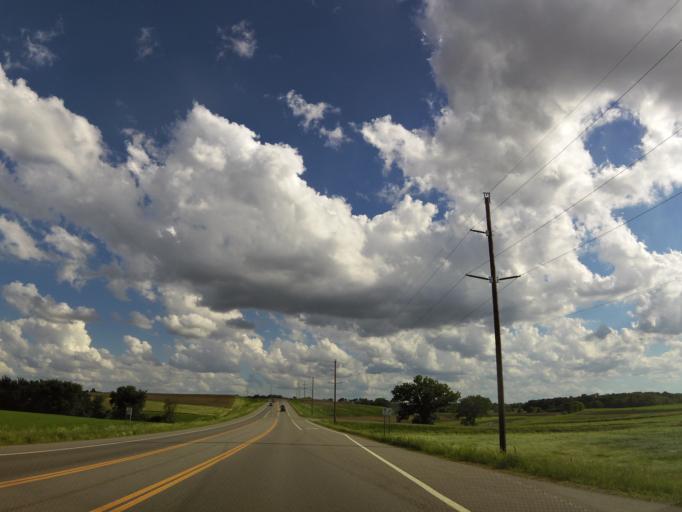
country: US
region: Minnesota
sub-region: Carver County
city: Waconia
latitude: 44.8924
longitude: -93.8186
